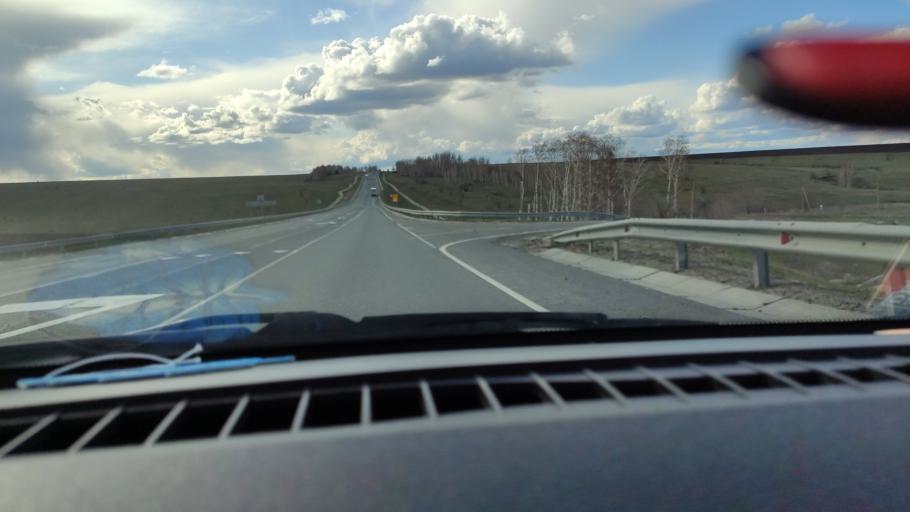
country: RU
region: Saratov
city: Shikhany
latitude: 52.1197
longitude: 47.2670
